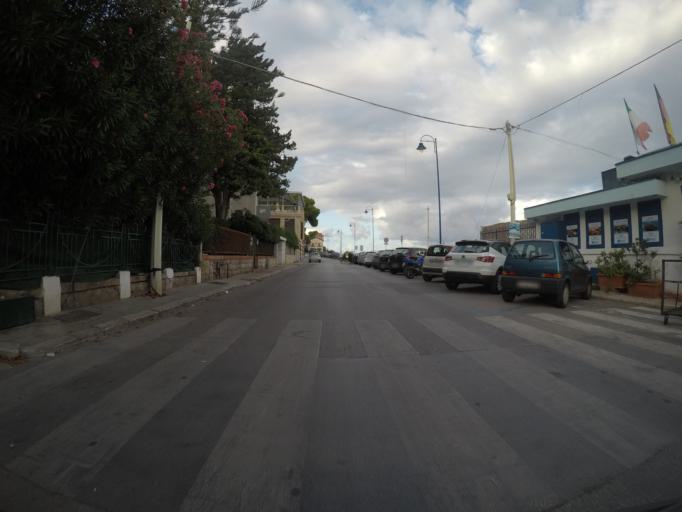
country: IT
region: Sicily
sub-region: Palermo
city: Palermo
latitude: 38.2082
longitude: 13.3284
